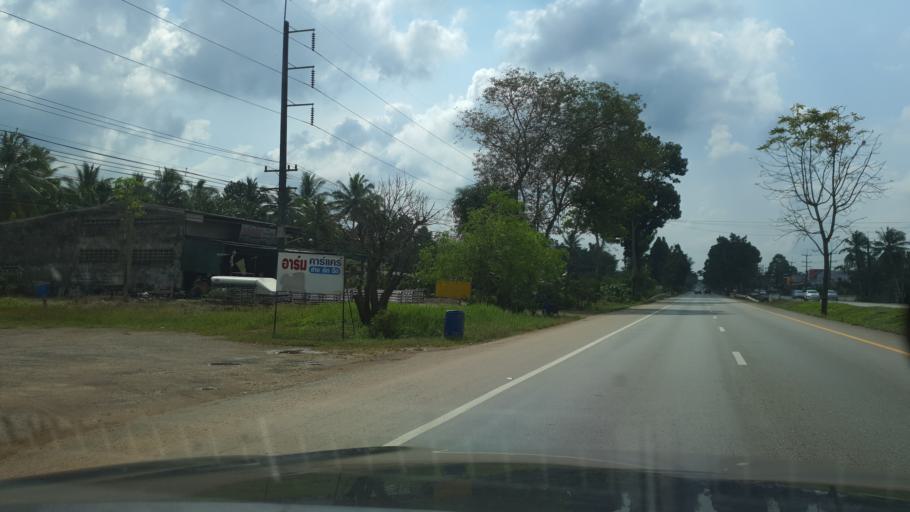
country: TH
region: Chumphon
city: Tha Sae
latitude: 10.6841
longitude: 99.2041
